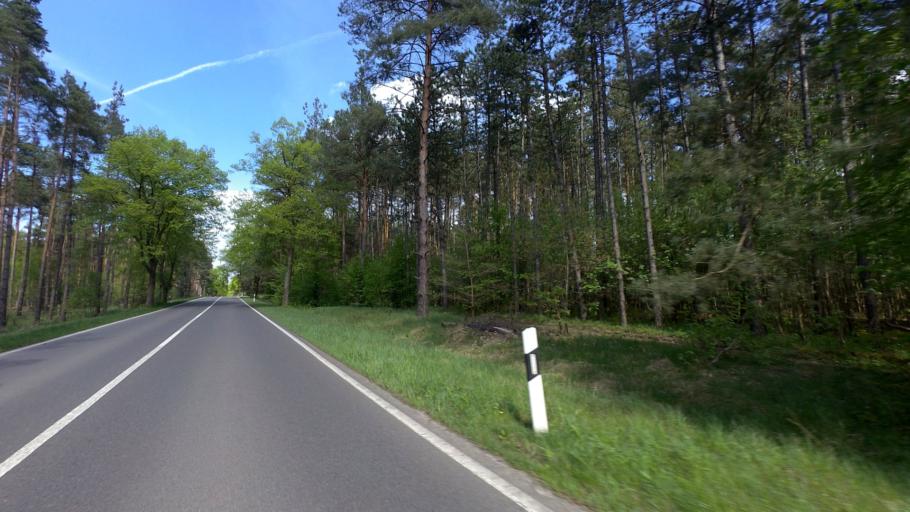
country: DE
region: Brandenburg
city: Milmersdorf
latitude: 53.0865
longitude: 13.6257
